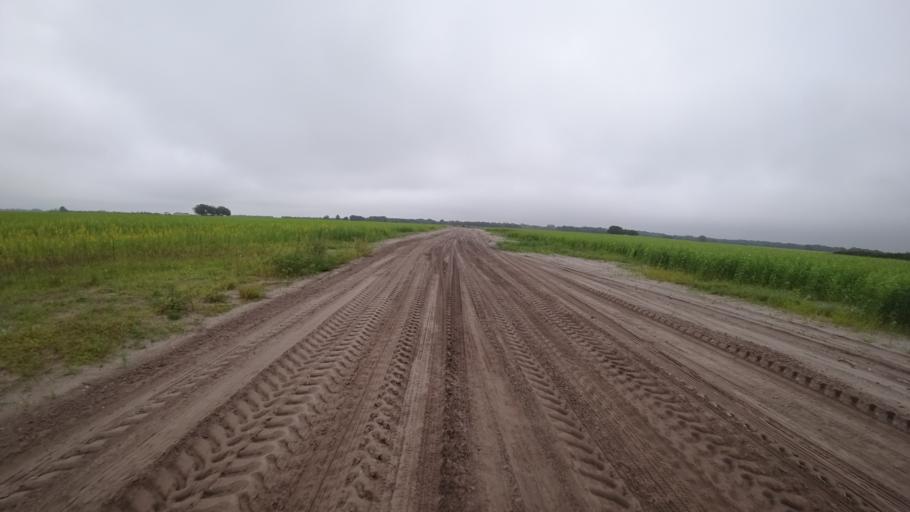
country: US
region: Florida
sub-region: Sarasota County
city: Warm Mineral Springs
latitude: 27.2904
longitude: -82.1622
